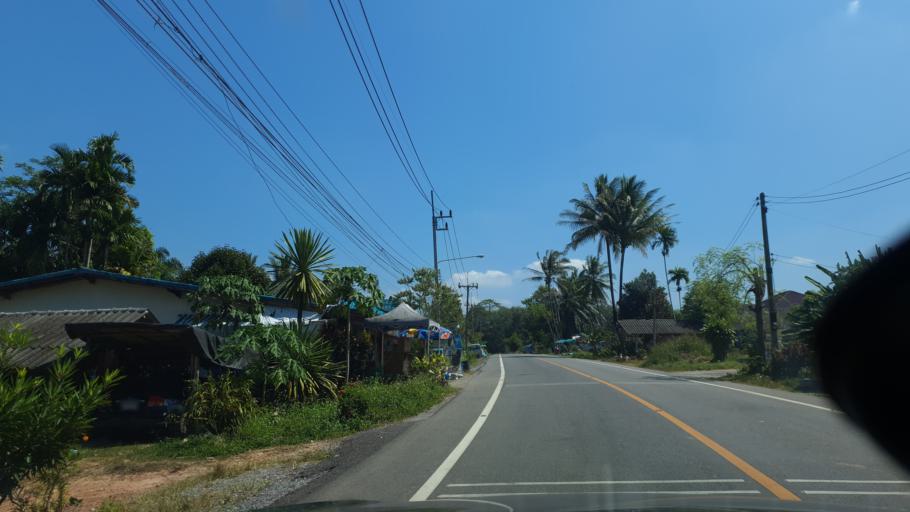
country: TH
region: Krabi
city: Khlong Thom
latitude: 7.9223
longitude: 99.2453
